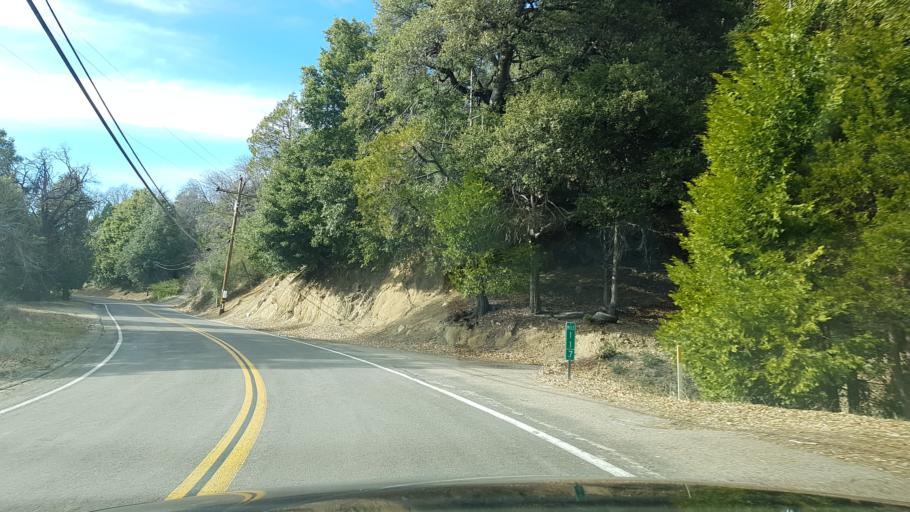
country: US
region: California
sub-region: Riverside County
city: Aguanga
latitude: 33.3161
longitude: -116.8701
